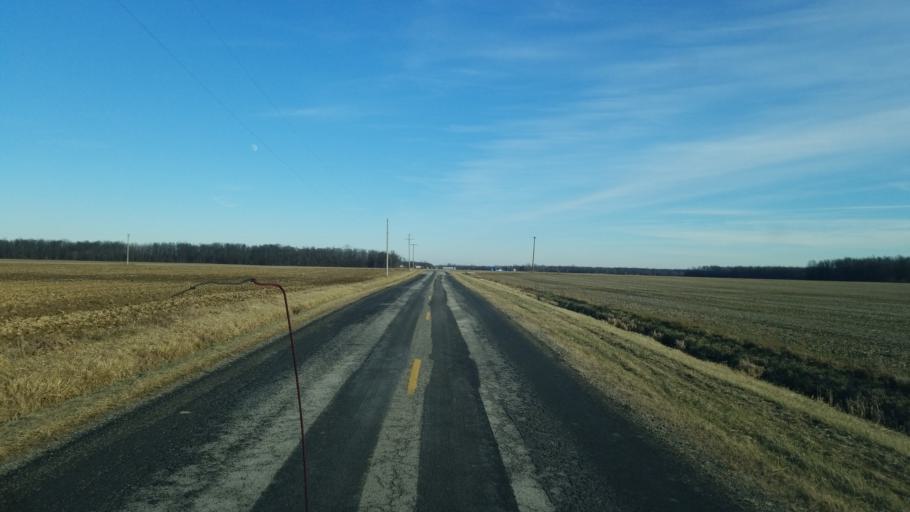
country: US
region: Ohio
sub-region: Huron County
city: Bellevue
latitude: 41.1799
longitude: -82.8093
